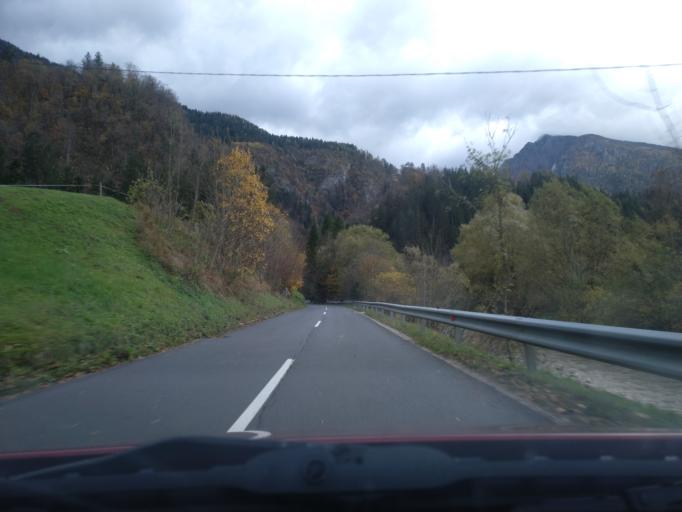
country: SI
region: Luce
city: Luce
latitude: 46.3635
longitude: 14.7340
